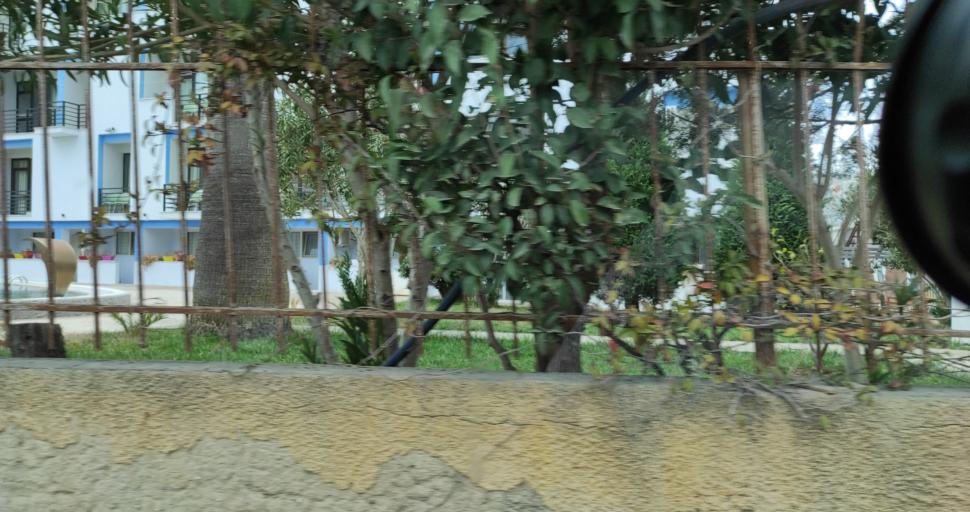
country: AL
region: Lezhe
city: Shengjin
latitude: 41.7962
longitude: 19.6053
